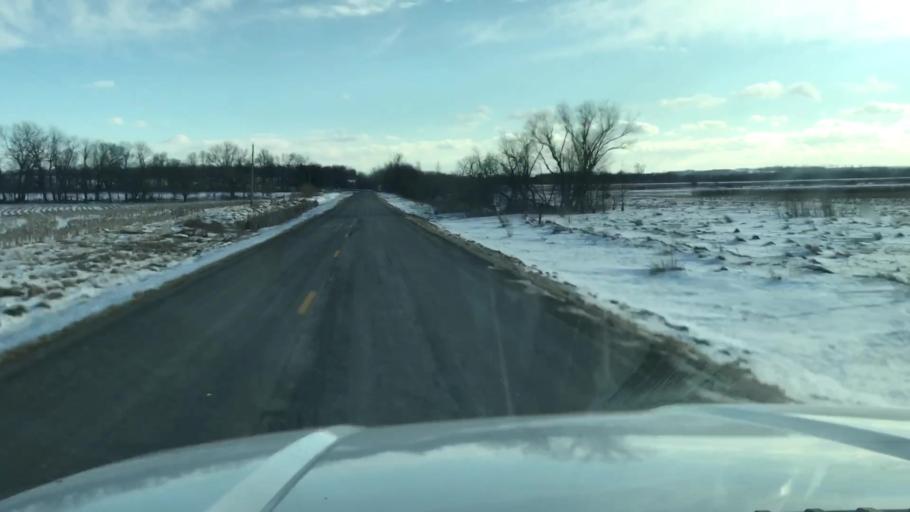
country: US
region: Missouri
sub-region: Holt County
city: Oregon
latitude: 40.1078
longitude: -95.0226
